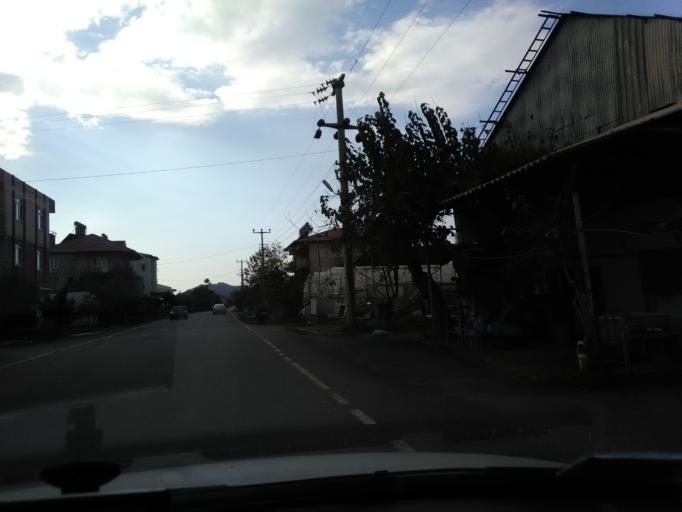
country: TR
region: Antalya
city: Gazipasa
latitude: 36.2712
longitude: 32.3316
